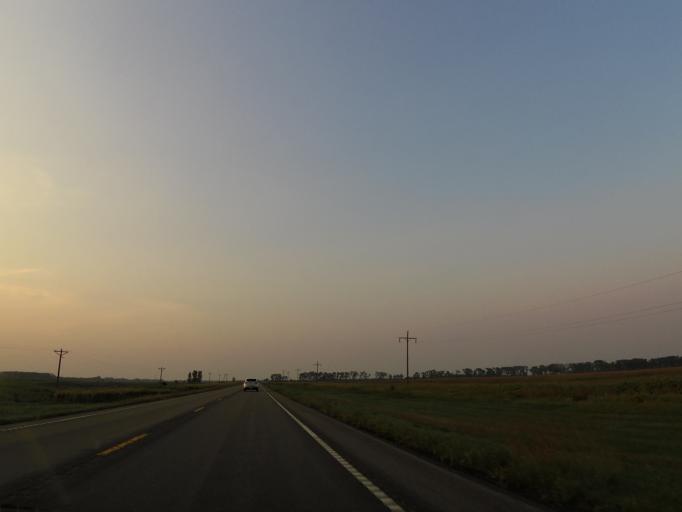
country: US
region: North Dakota
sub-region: Grand Forks County
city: Larimore
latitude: 48.1465
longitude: -97.6225
